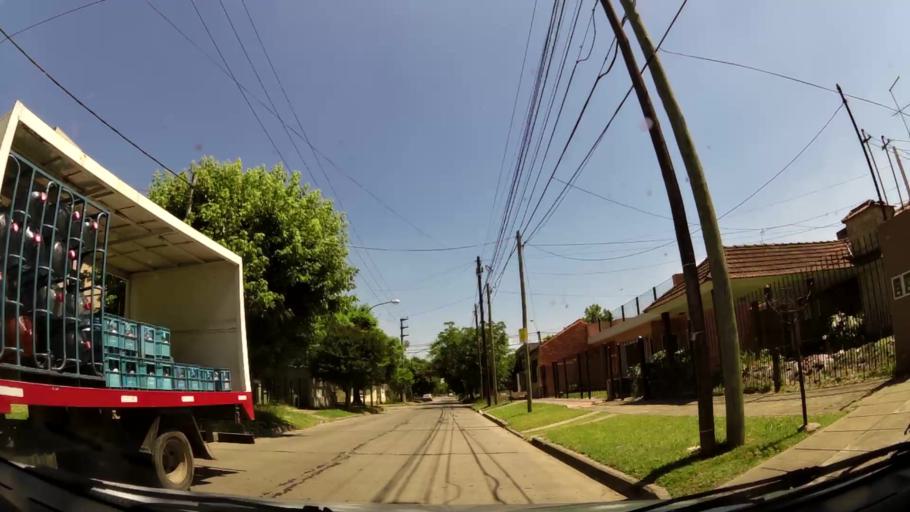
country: AR
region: Buenos Aires
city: Ituzaingo
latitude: -34.6560
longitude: -58.6806
